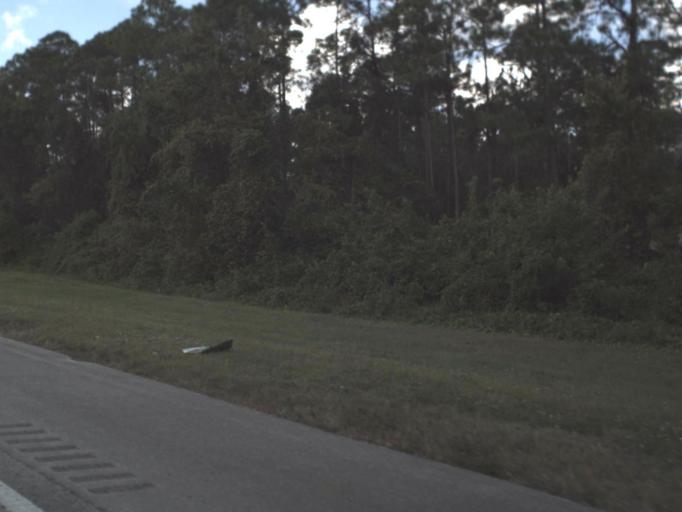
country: US
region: Florida
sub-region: Indian River County
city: Fellsmere
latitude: 27.5637
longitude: -80.7821
